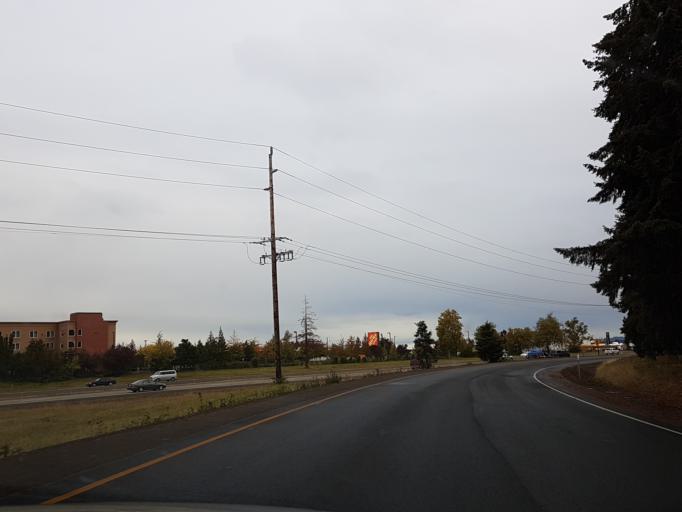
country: US
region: Oregon
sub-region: Linn County
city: Albany
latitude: 44.6288
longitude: -123.0634
